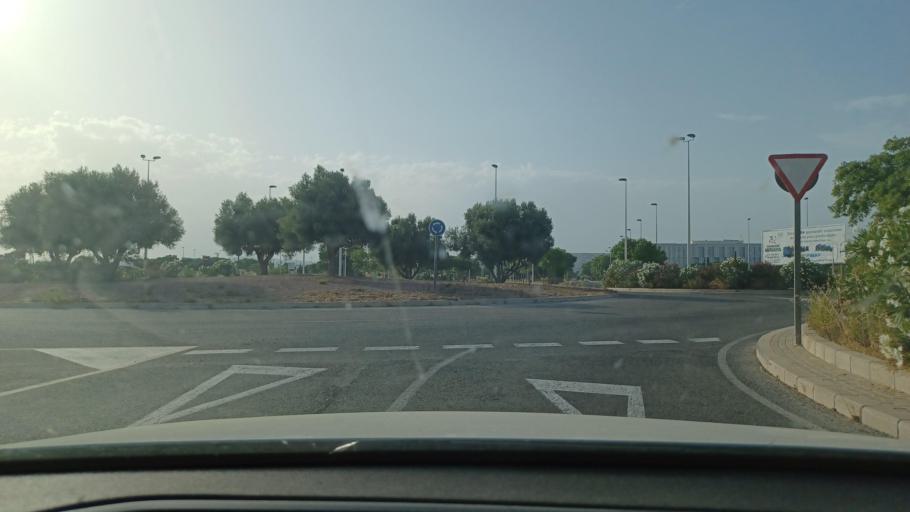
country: ES
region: Valencia
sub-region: Provincia de Alicante
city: Elche
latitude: 38.2862
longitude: -0.6239
